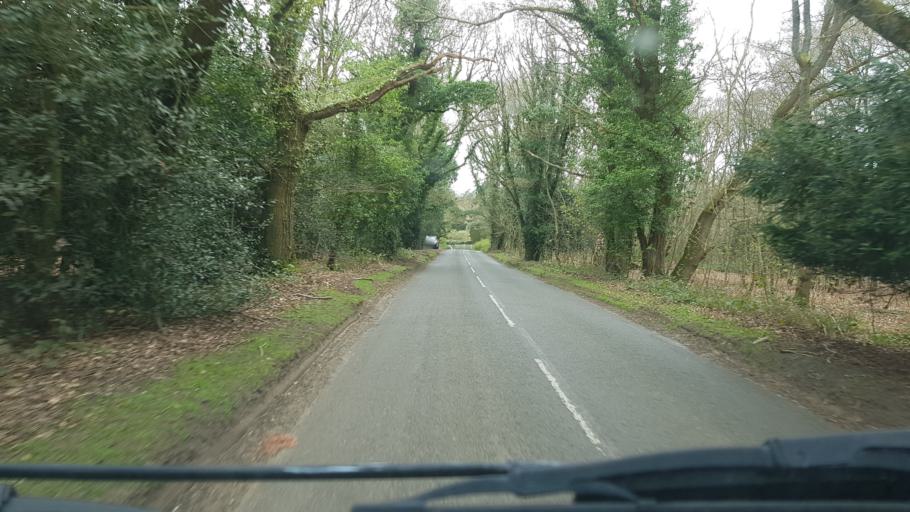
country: GB
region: England
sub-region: Surrey
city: Chilworth
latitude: 51.2114
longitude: -0.4736
